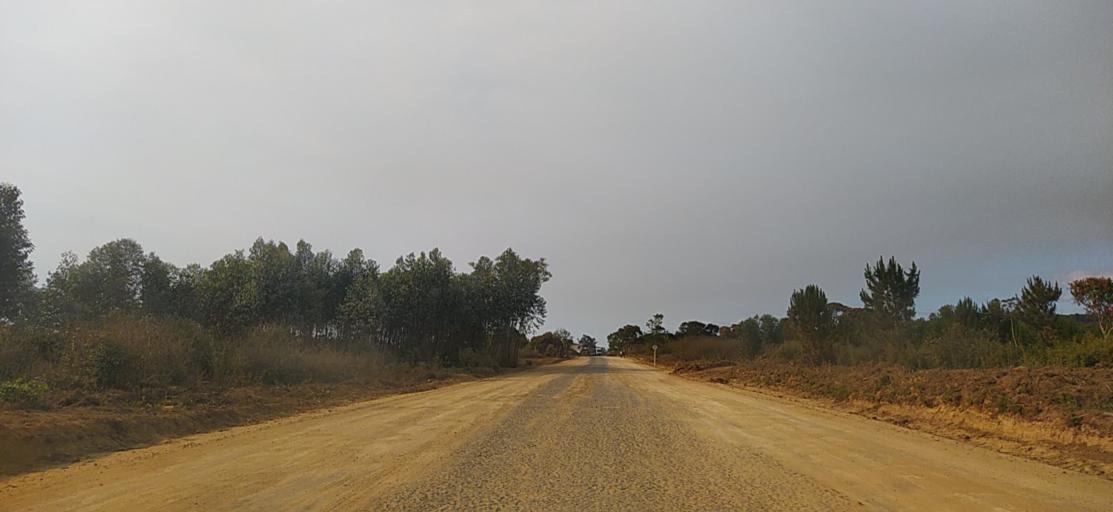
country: MG
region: Alaotra Mangoro
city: Moramanga
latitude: -18.6390
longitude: 48.2758
